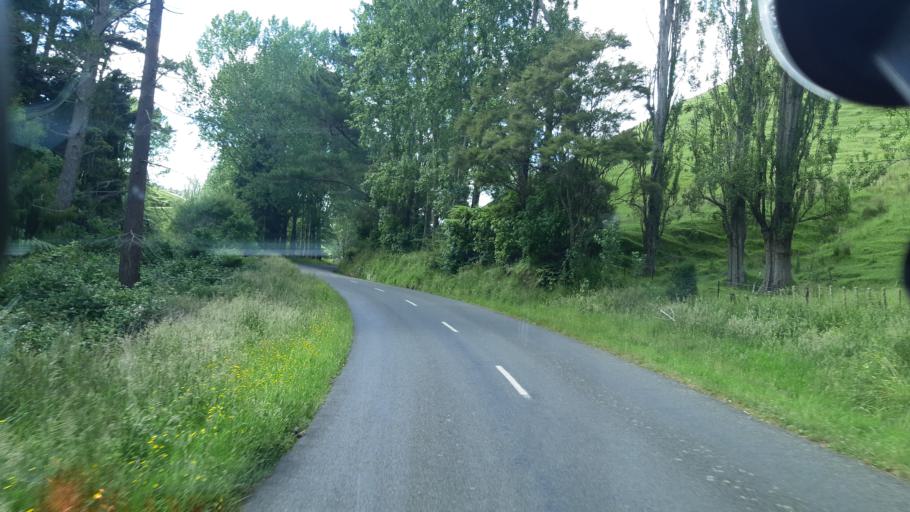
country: NZ
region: Manawatu-Wanganui
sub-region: Rangitikei District
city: Bulls
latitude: -39.9214
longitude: 175.5564
